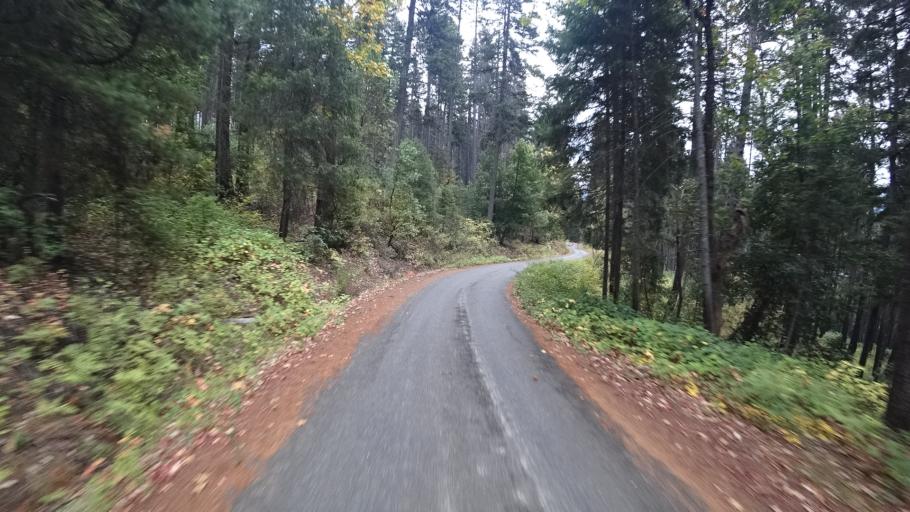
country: US
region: California
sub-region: Siskiyou County
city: Happy Camp
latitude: 41.8026
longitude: -123.3396
